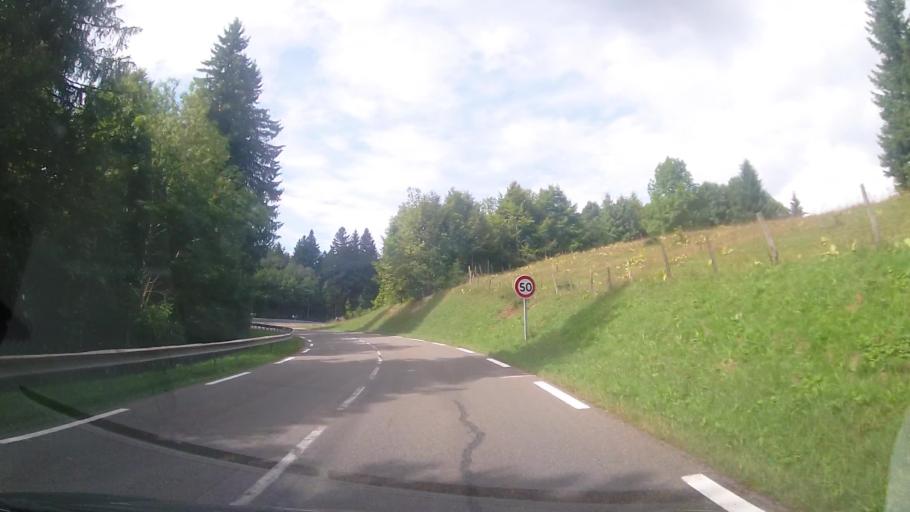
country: FR
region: Franche-Comte
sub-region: Departement du Jura
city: Les Rousses
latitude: 46.4134
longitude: 6.0609
